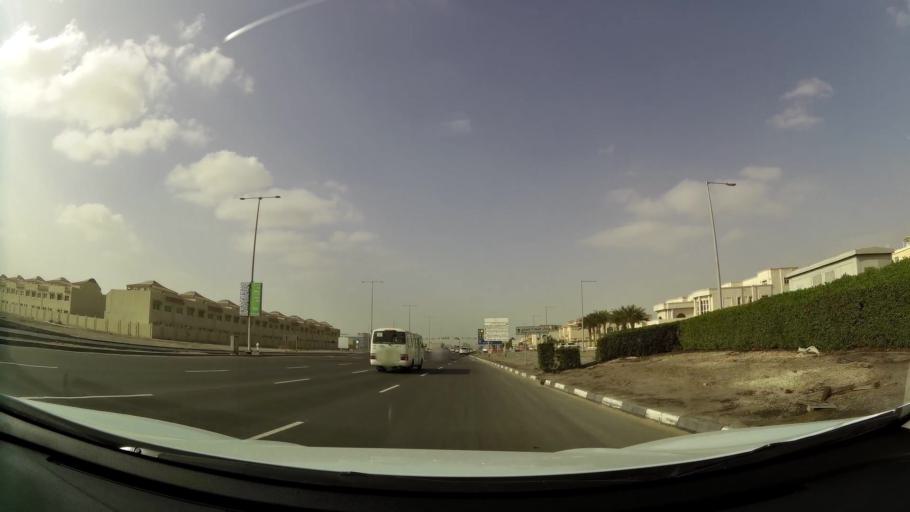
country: AE
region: Abu Dhabi
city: Abu Dhabi
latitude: 24.4017
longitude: 54.5730
